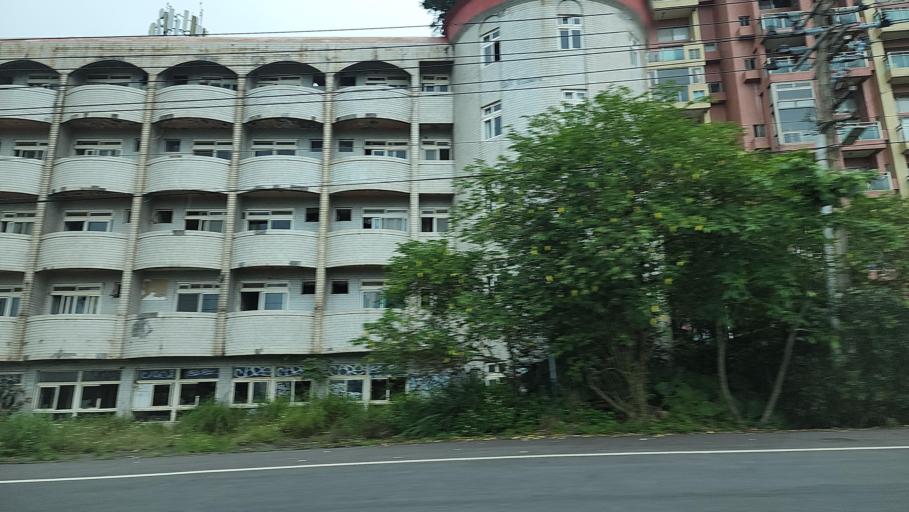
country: TW
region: Taiwan
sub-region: Keelung
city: Keelung
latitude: 25.1927
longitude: 121.6802
